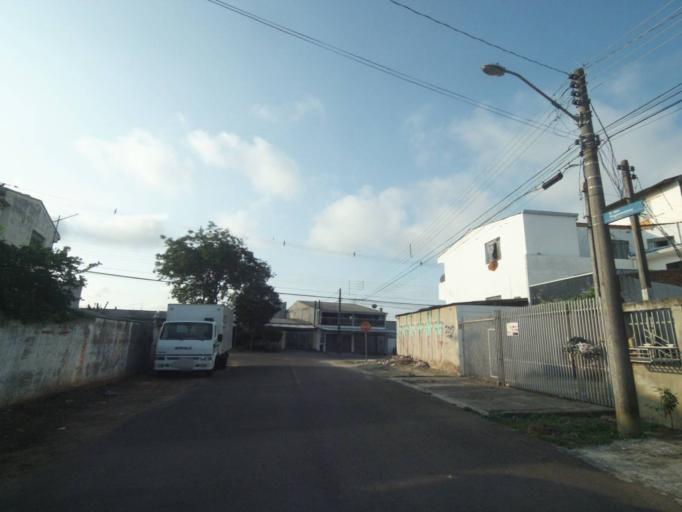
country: BR
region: Parana
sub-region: Sao Jose Dos Pinhais
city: Sao Jose dos Pinhais
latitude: -25.5438
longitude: -49.2484
